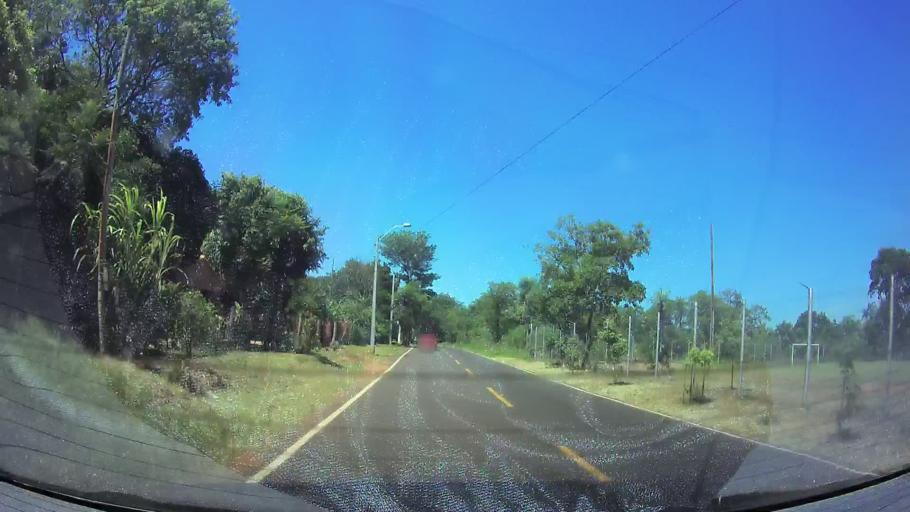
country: PY
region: Central
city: Aregua
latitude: -25.2523
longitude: -57.4428
